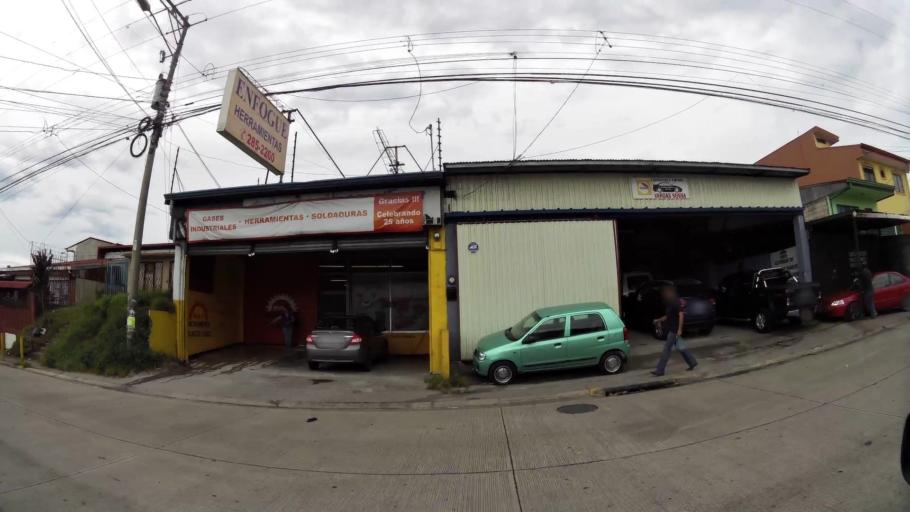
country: CR
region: San Jose
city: Purral
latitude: 9.9614
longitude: -84.0364
